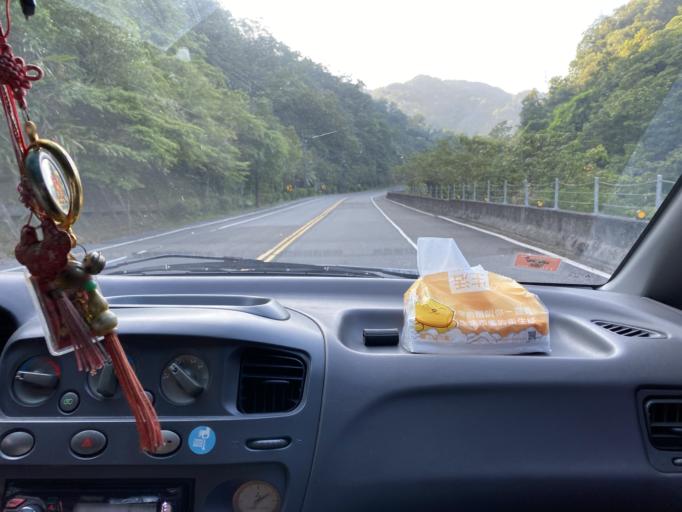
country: TW
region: Taiwan
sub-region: Keelung
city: Keelung
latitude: 25.0297
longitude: 121.7797
